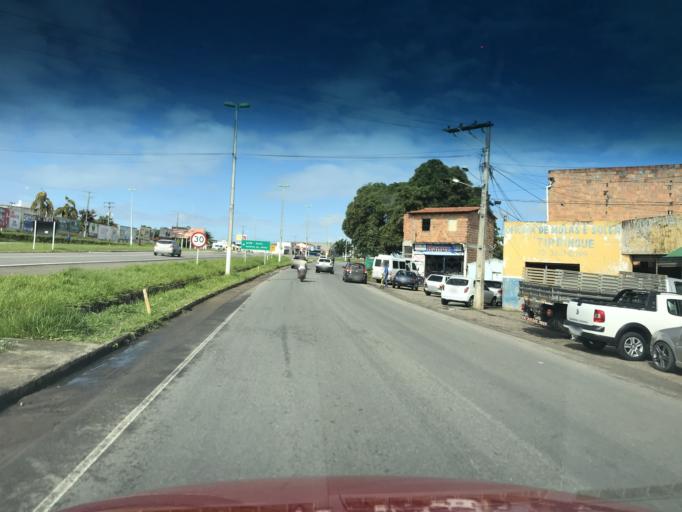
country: BR
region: Bahia
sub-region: Santo Antonio De Jesus
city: Santo Antonio de Jesus
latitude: -12.9679
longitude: -39.2732
